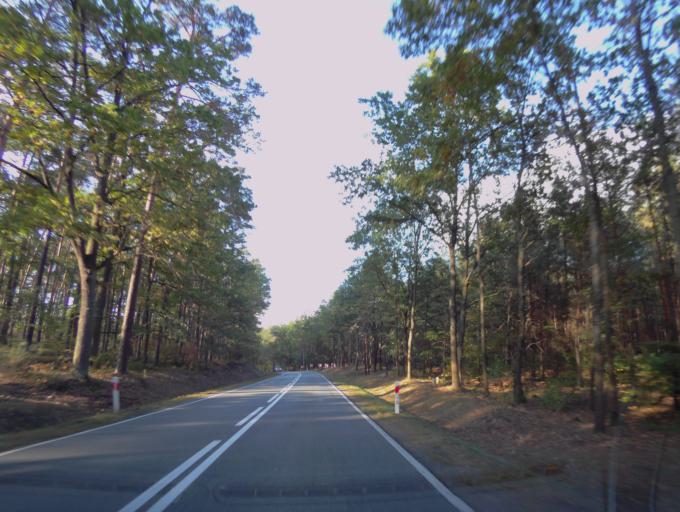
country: PL
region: Subcarpathian Voivodeship
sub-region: Powiat nizanski
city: Krzeszow
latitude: 50.3845
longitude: 22.3083
